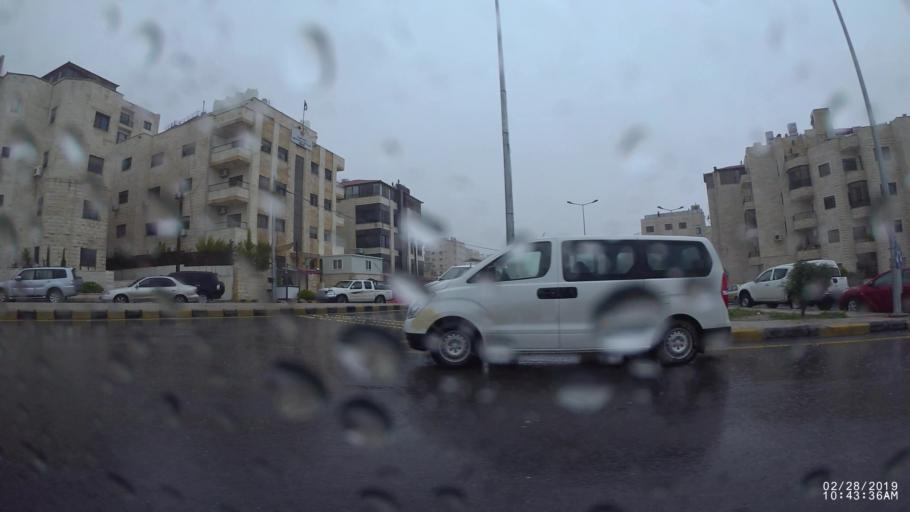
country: JO
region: Amman
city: Al Jubayhah
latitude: 32.0166
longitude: 35.8893
